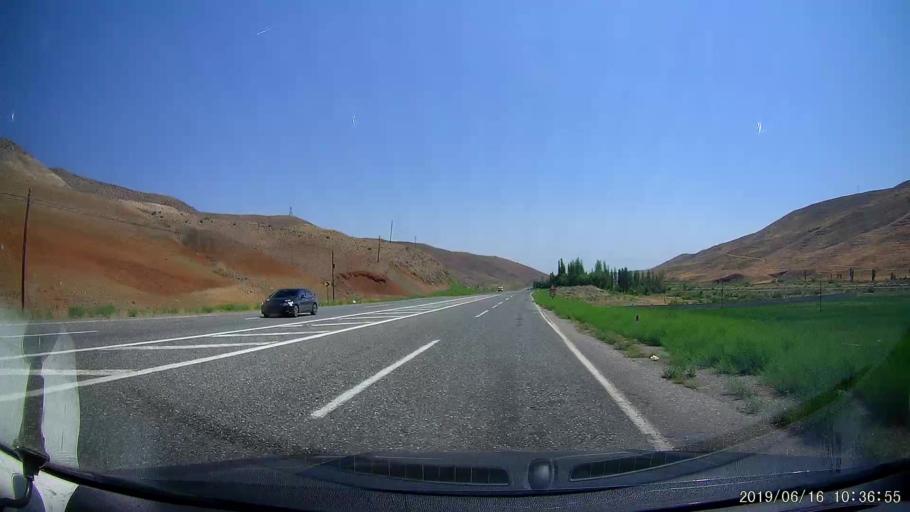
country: TR
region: Igdir
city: Tuzluca
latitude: 40.0430
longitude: 43.6888
